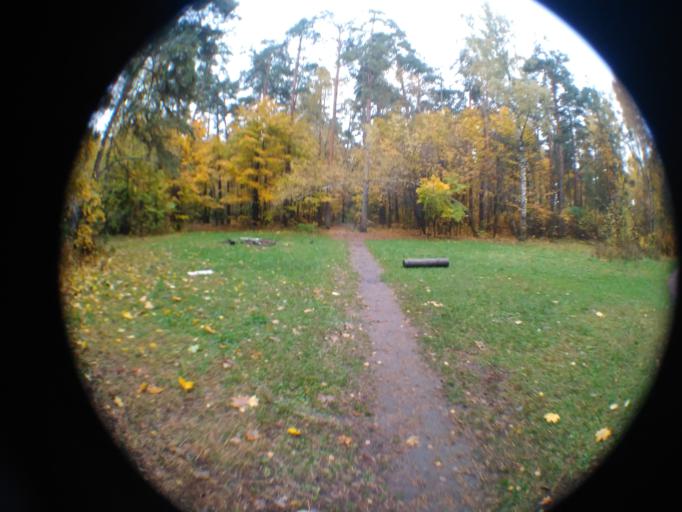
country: RU
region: Moskovskaya
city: Zhukovskiy
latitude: 55.5835
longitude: 38.1268
